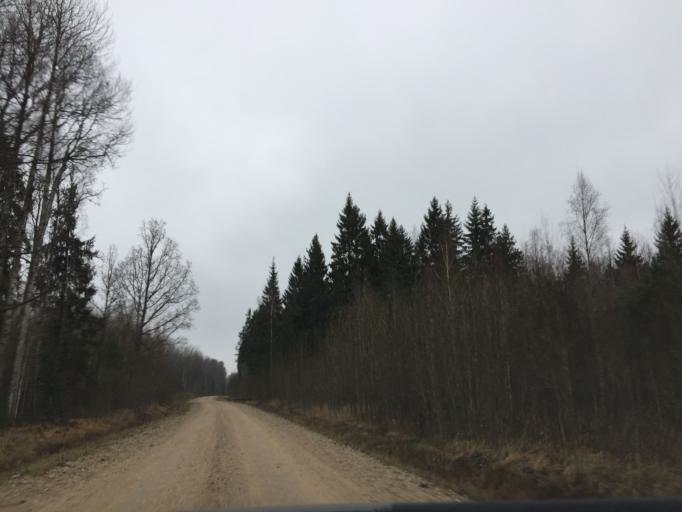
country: LV
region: Limbazu Rajons
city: Limbazi
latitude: 57.4856
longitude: 24.7607
